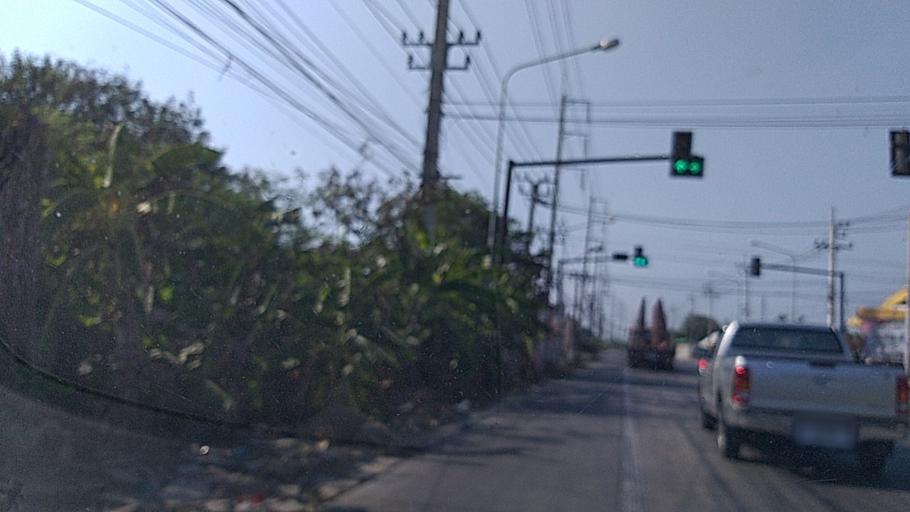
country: TH
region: Nonthaburi
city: Sai Noi
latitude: 13.9089
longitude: 100.3235
